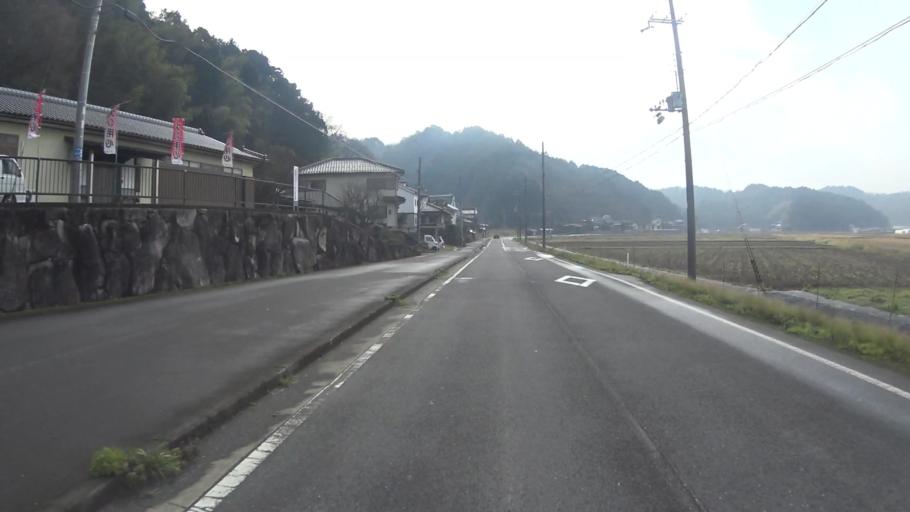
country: JP
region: Kyoto
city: Maizuru
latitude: 35.4606
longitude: 135.2876
